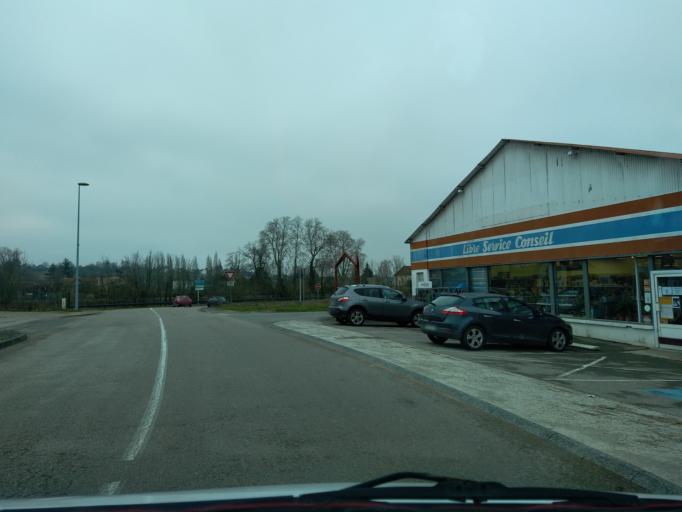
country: FR
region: Franche-Comte
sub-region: Departement de la Haute-Saone
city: Arc-les-Gray
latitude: 47.4508
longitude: 5.5780
